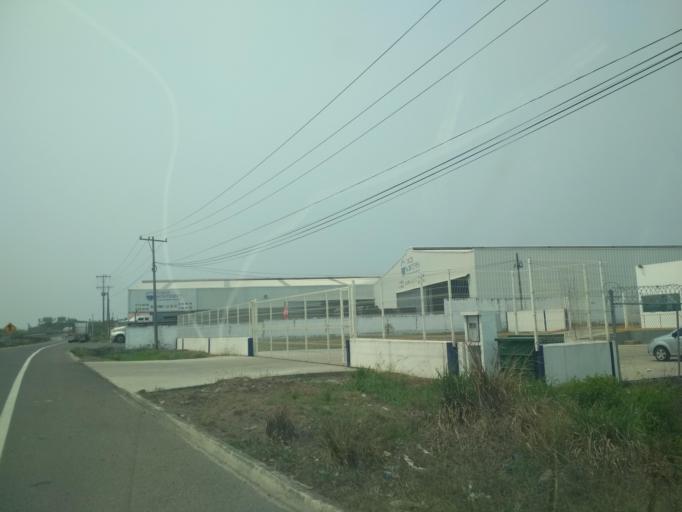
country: MX
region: Veracruz
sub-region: Veracruz
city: Delfino Victoria (Santa Fe)
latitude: 19.1915
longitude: -96.2752
